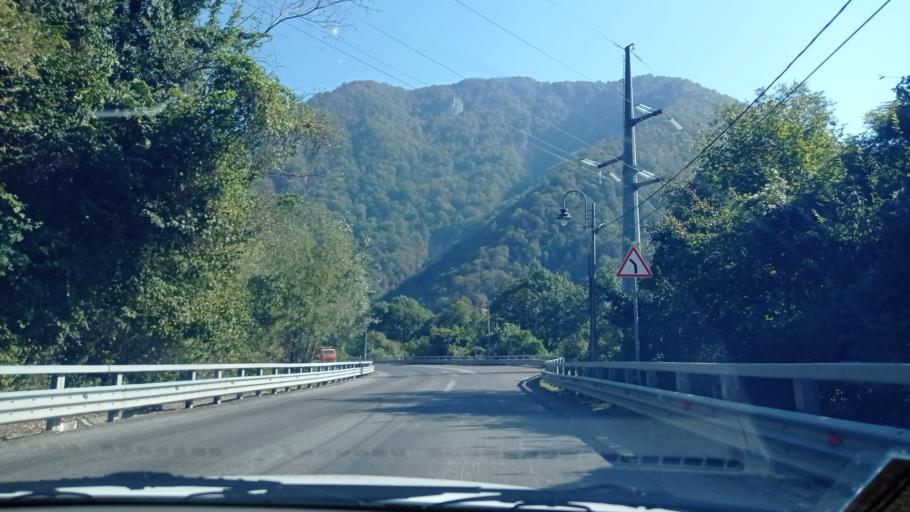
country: RU
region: Krasnodarskiy
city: Vysokoye
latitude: 43.5932
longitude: 40.0119
